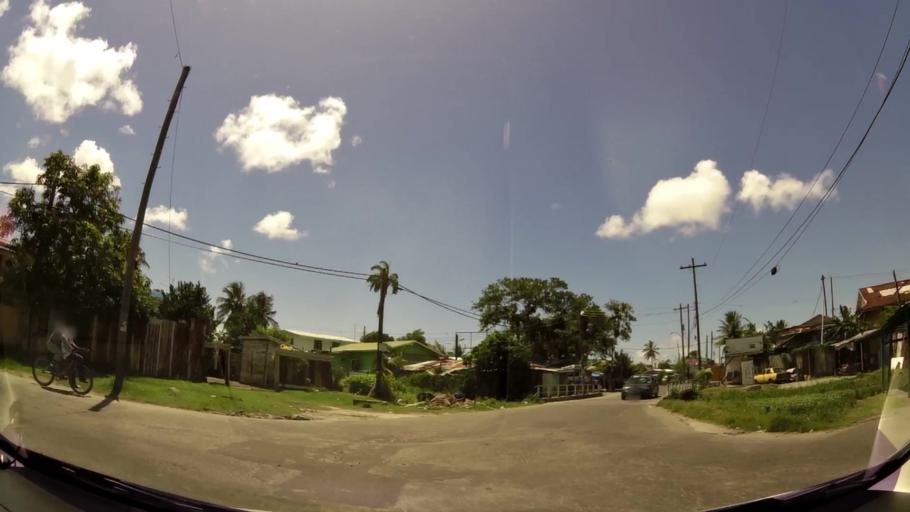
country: GY
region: Demerara-Mahaica
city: Georgetown
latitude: 6.7960
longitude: -58.1641
